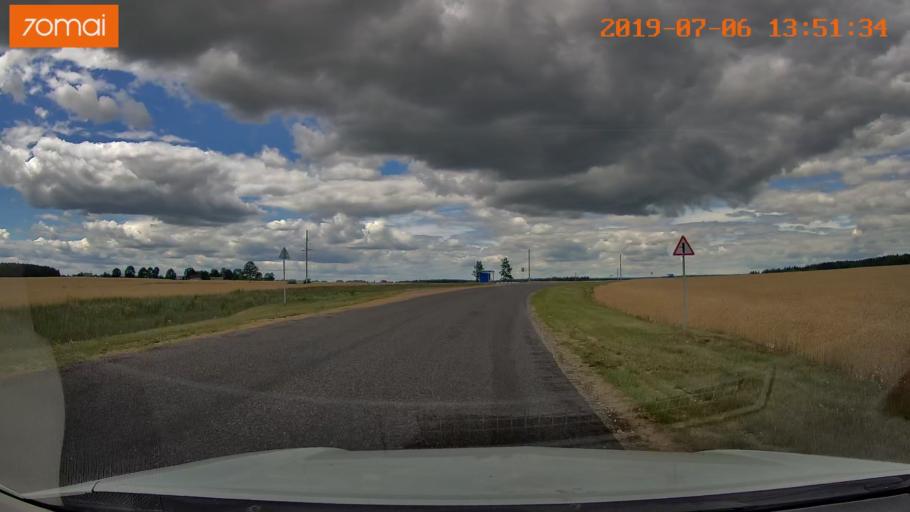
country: BY
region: Minsk
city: Ivyanyets
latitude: 53.7096
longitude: 26.8299
